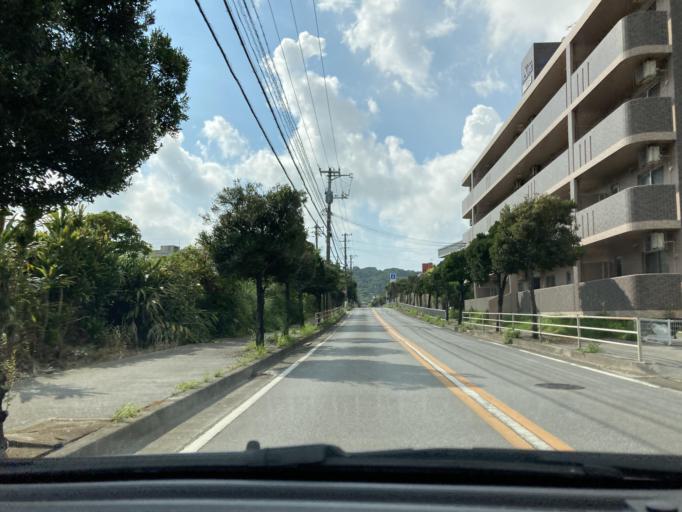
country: JP
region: Okinawa
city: Tomigusuku
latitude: 26.1550
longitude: 127.7500
